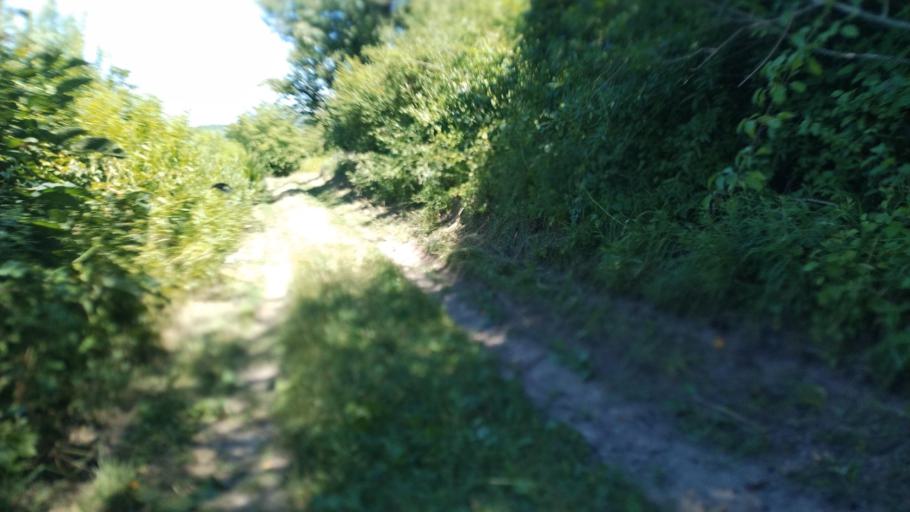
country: DE
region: Baden-Wuerttemberg
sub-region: Karlsruhe Region
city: Ubstadt-Weiher
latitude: 49.1413
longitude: 8.6475
